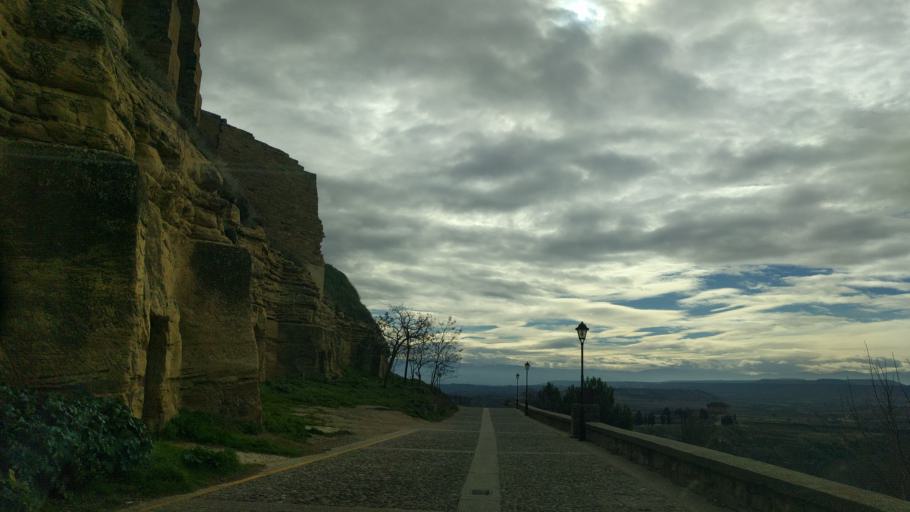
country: ES
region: La Rioja
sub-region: Provincia de La Rioja
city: San Vicente de la Sonsierra
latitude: 42.5596
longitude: -2.7583
